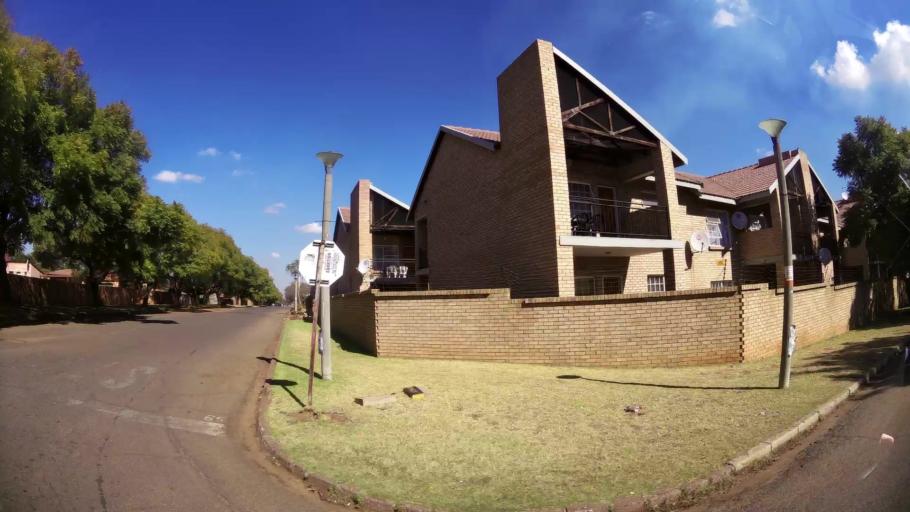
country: ZA
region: Mpumalanga
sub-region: Nkangala District Municipality
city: Witbank
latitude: -25.8705
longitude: 29.2192
